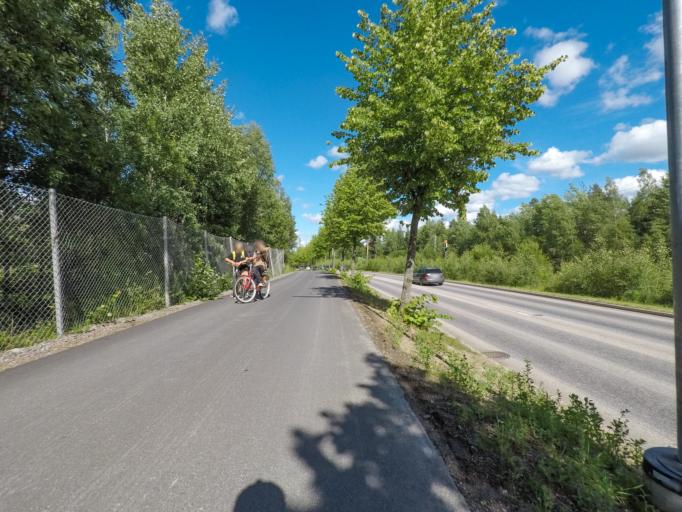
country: FI
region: South Karelia
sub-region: Lappeenranta
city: Lappeenranta
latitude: 61.0612
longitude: 28.2494
